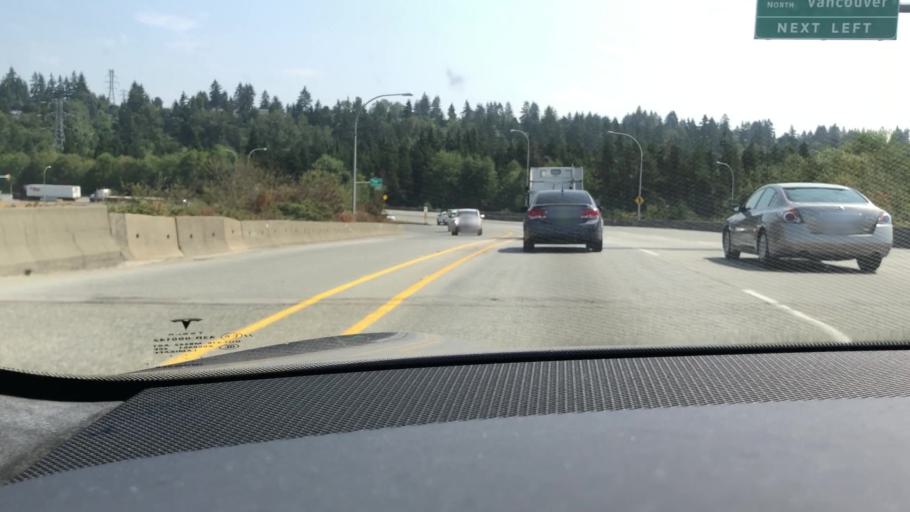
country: CA
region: British Columbia
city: Delta
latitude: 49.1455
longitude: -122.9362
